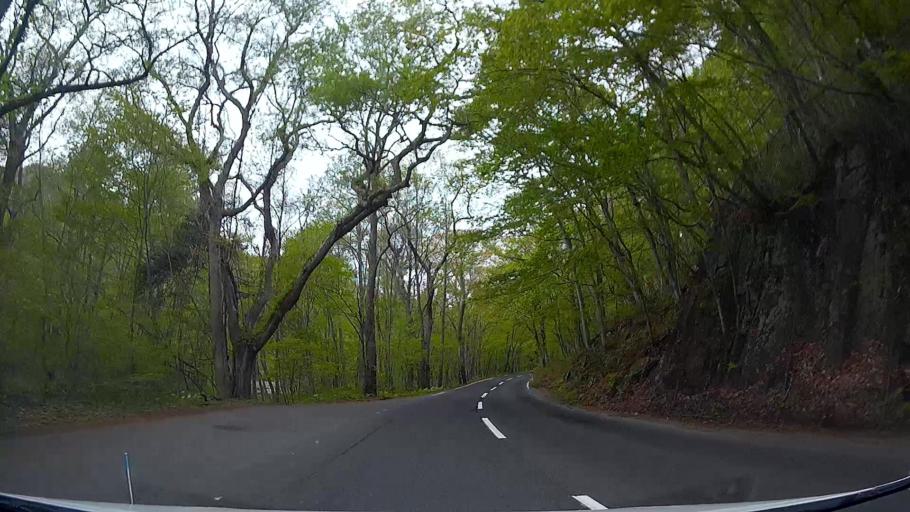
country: JP
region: Aomori
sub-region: Aomori Shi
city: Furudate
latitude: 40.5714
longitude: 140.9787
